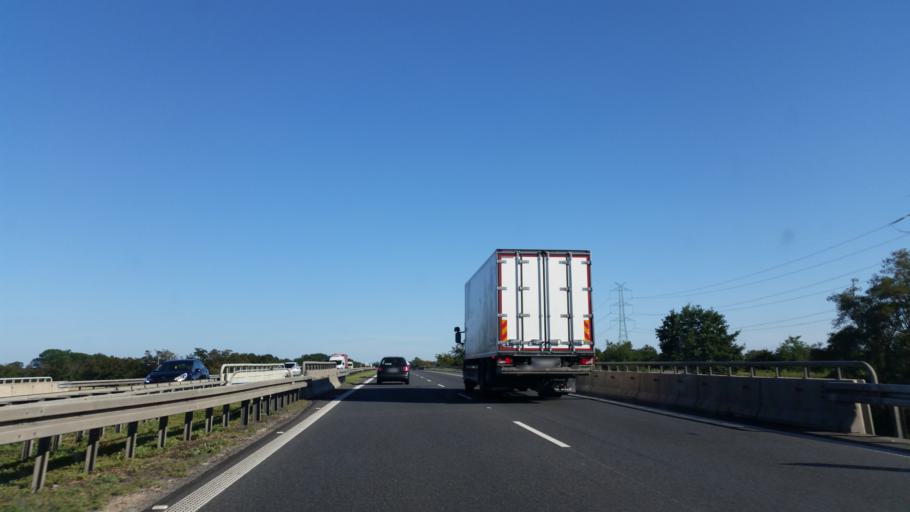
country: PL
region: Lower Silesian Voivodeship
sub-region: Powiat strzelinski
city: Wiazow
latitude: 50.8276
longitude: 17.2934
